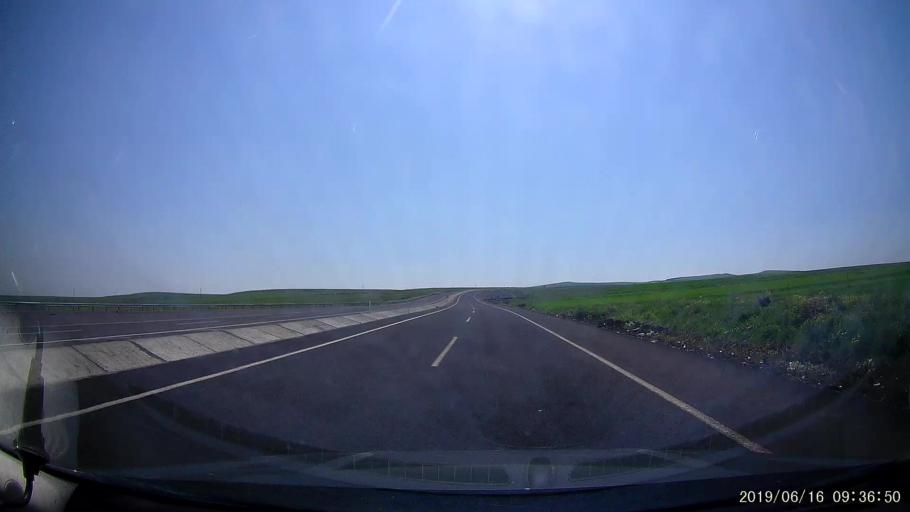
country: TR
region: Kars
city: Kars
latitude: 40.5556
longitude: 43.1812
